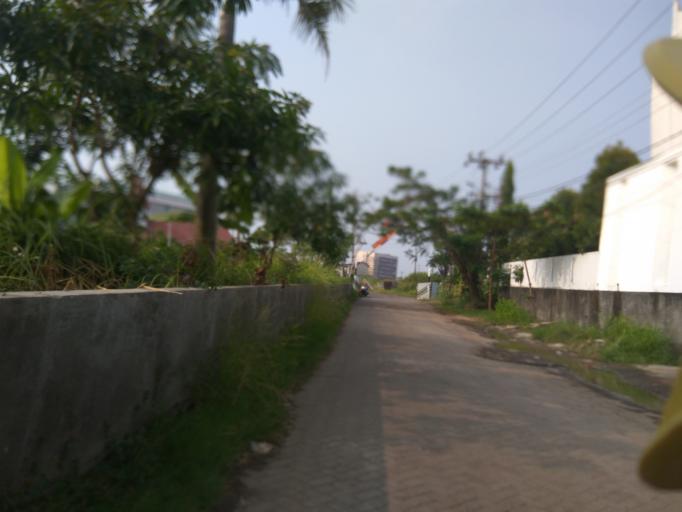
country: ID
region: Central Java
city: Semarang
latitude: -6.9665
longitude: 110.3957
